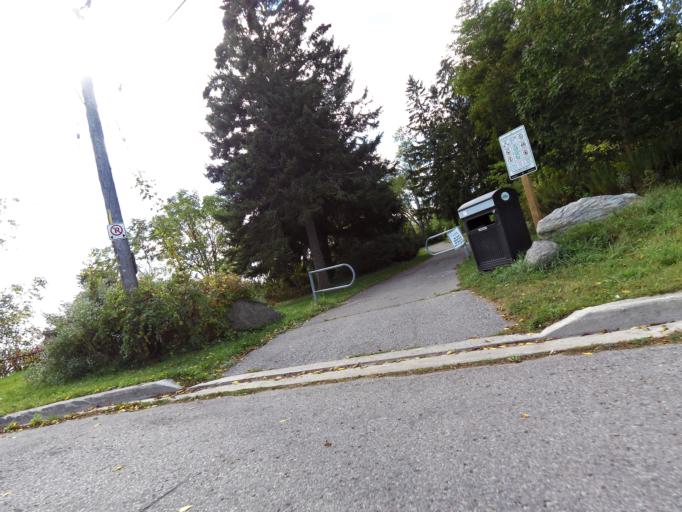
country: CA
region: Ontario
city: Ajax
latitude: 43.8068
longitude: -79.1011
